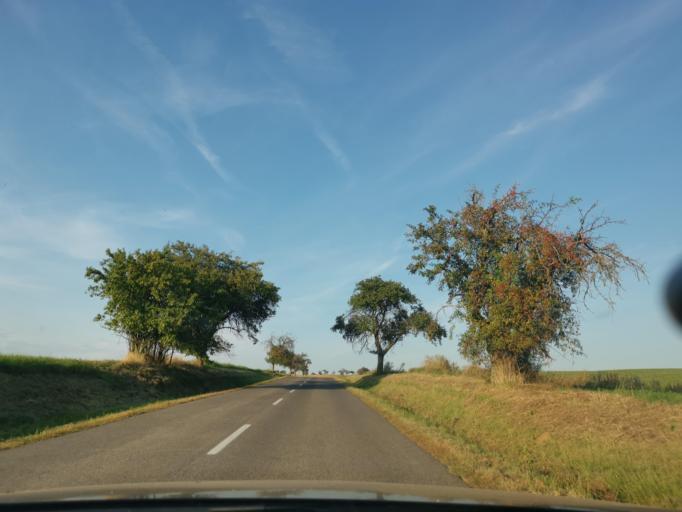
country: SK
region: Trnavsky
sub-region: Okres Senica
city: Senica
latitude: 48.7127
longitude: 17.2868
